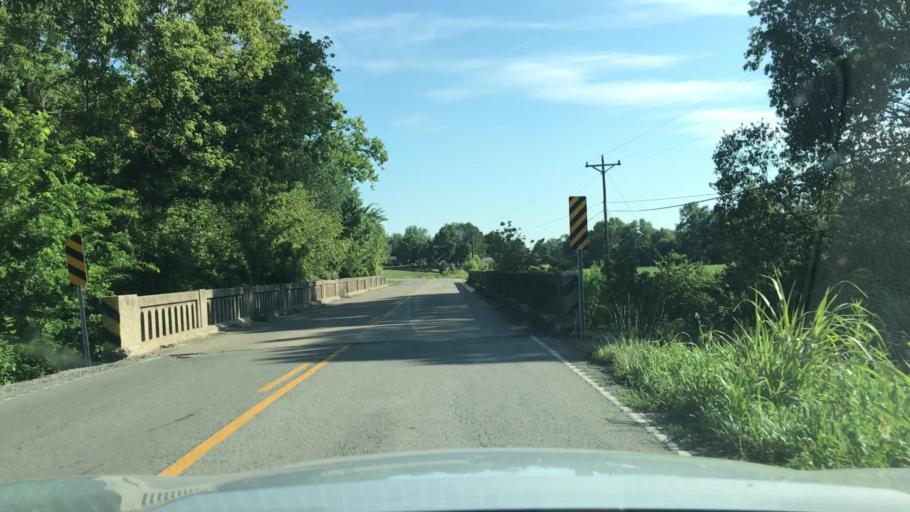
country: US
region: Kentucky
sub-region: Muhlenberg County
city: Greenville
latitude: 37.1434
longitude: -87.1417
